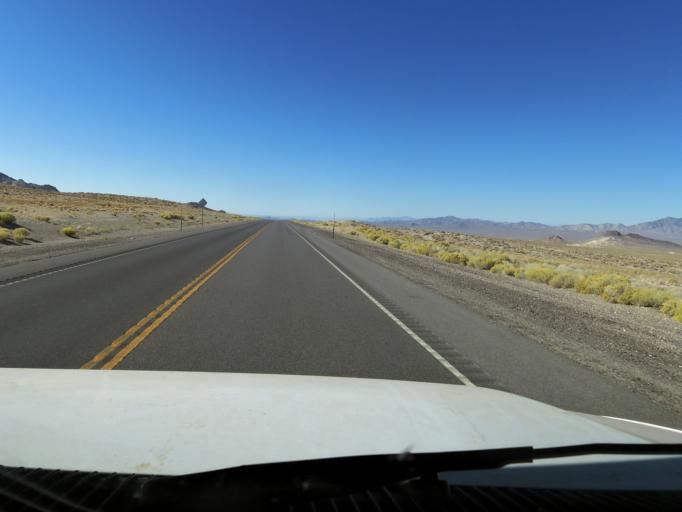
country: US
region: Nevada
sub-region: Nye County
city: Tonopah
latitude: 38.0294
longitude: -117.2350
